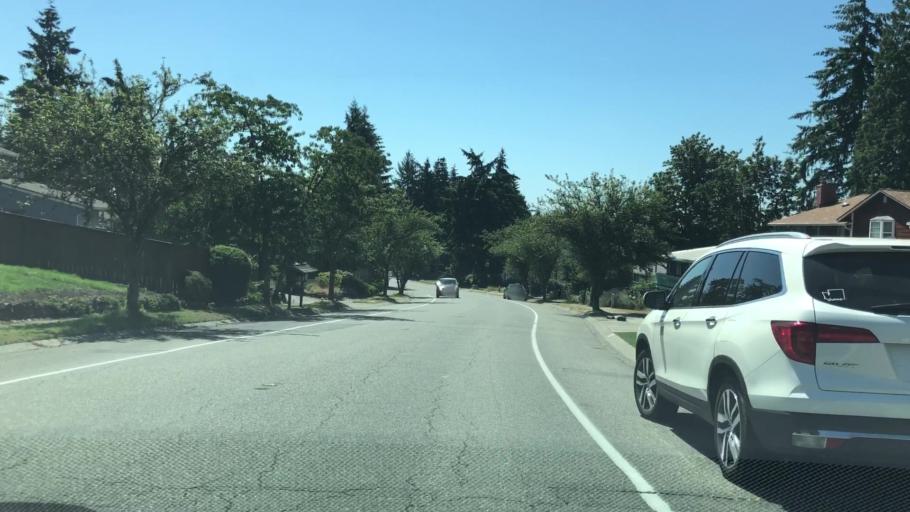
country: US
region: Washington
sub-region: King County
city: Kingsgate
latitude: 47.7245
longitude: -122.1866
